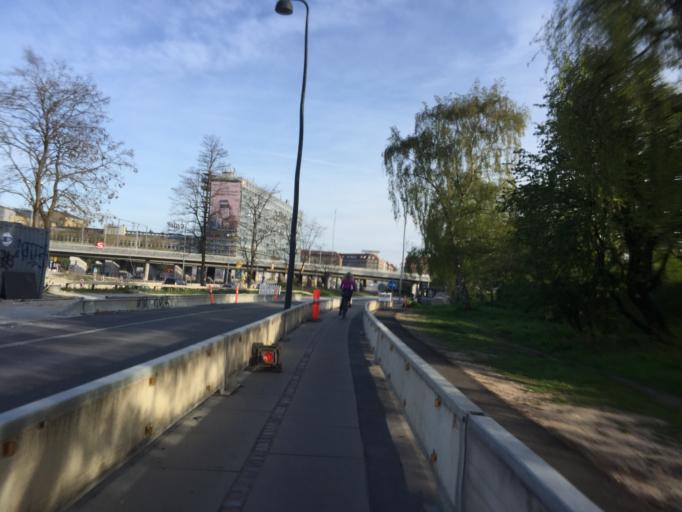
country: DK
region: Capital Region
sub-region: Kobenhavn
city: Copenhagen
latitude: 55.7162
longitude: 12.5576
